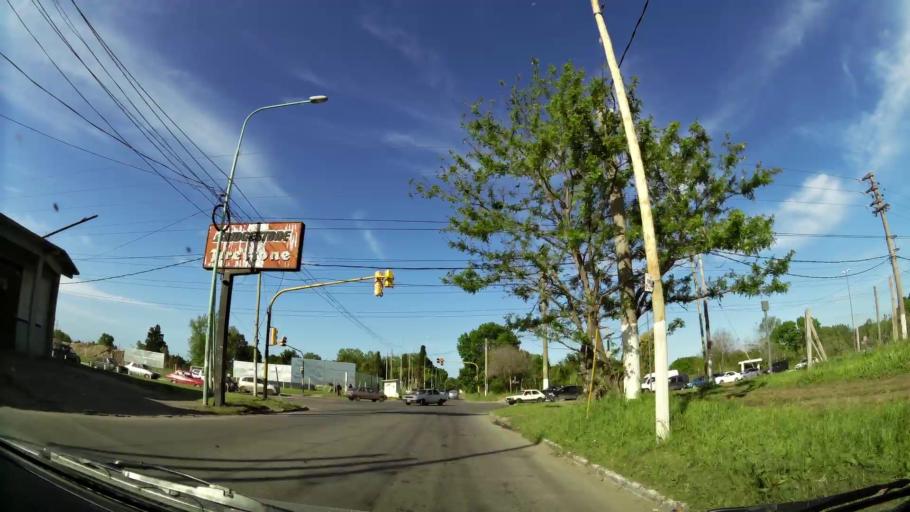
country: AR
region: Buenos Aires
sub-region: Partido de Quilmes
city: Quilmes
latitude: -34.7900
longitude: -58.2181
